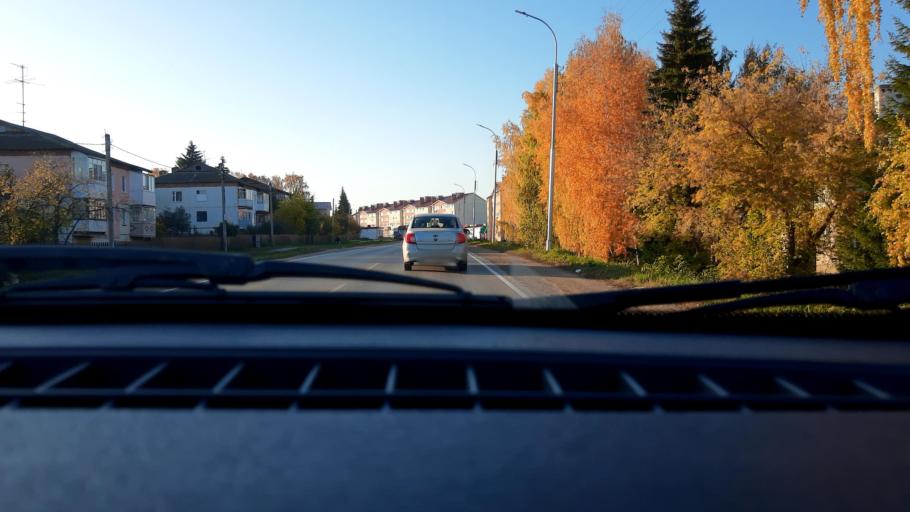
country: RU
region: Bashkortostan
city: Mikhaylovka
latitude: 54.8145
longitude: 55.8010
